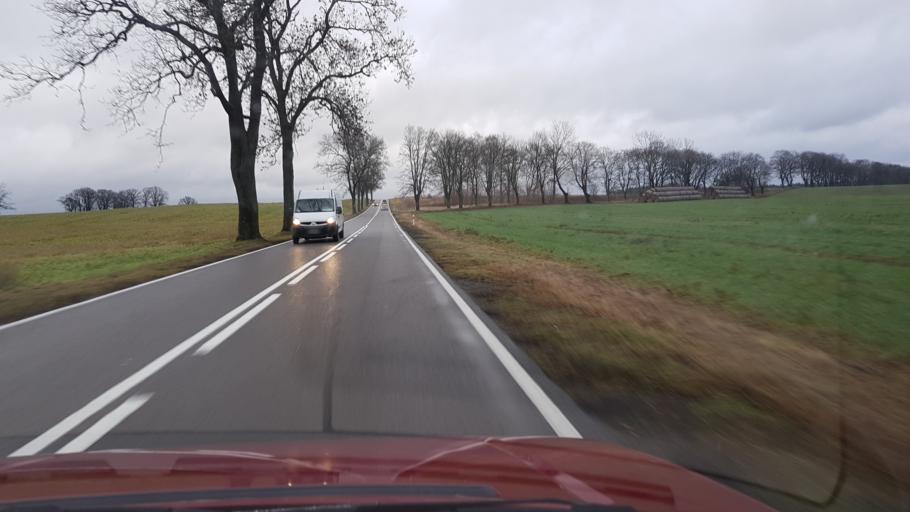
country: PL
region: West Pomeranian Voivodeship
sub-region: Powiat lobeski
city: Wegorzyno
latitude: 53.4988
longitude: 15.6715
